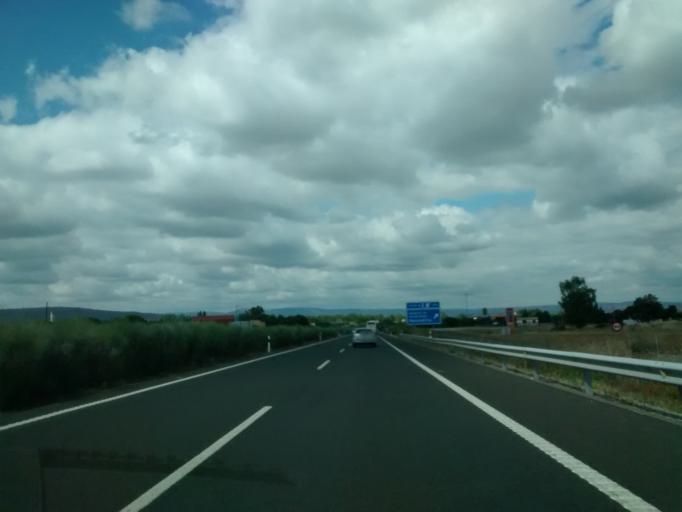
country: ES
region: Extremadura
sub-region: Provincia de Caceres
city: Millanes
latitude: 39.8599
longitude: -5.6125
